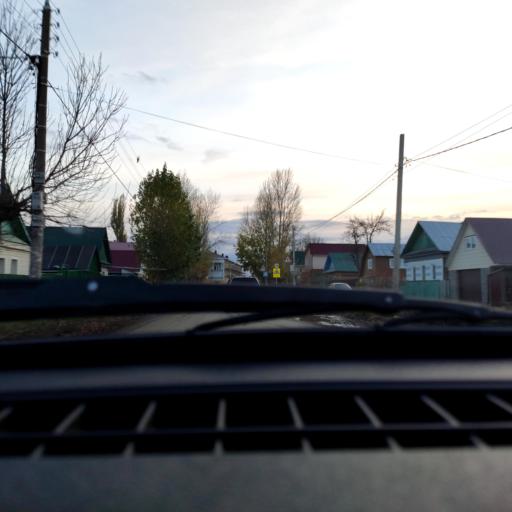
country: RU
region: Bashkortostan
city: Ufa
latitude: 54.7432
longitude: 55.9139
